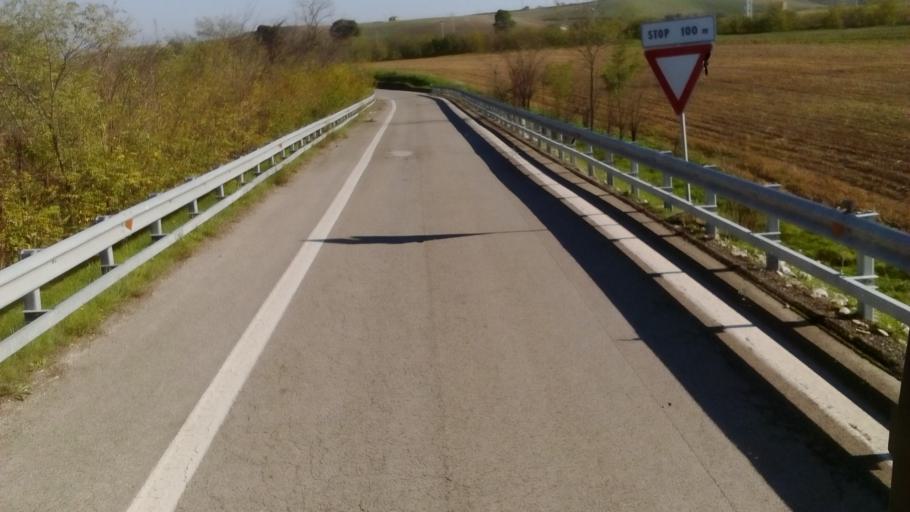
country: IT
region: Basilicate
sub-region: Provincia di Potenza
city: Melfi
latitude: 41.0650
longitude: 15.6769
